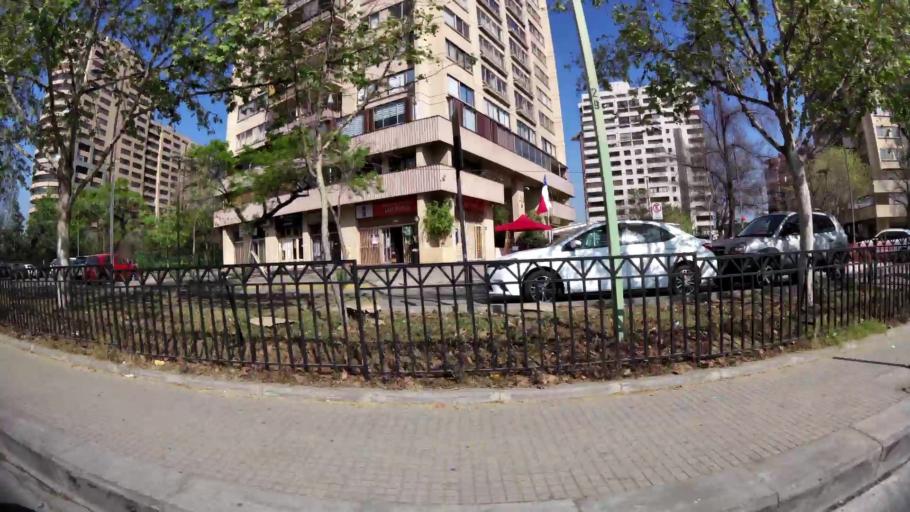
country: CL
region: Santiago Metropolitan
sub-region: Provincia de Santiago
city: Villa Presidente Frei, Nunoa, Santiago, Chile
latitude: -33.4049
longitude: -70.5849
